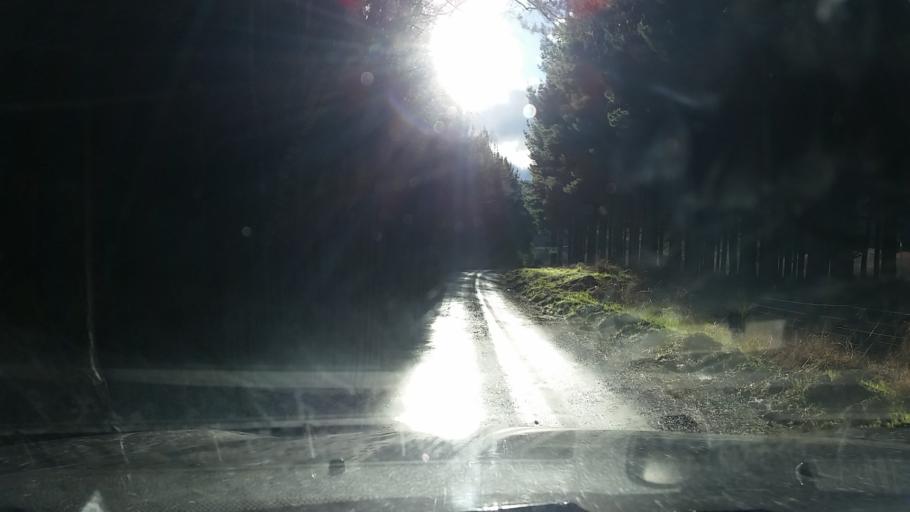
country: NZ
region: Nelson
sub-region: Nelson City
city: Nelson
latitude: -41.5532
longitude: 173.4237
